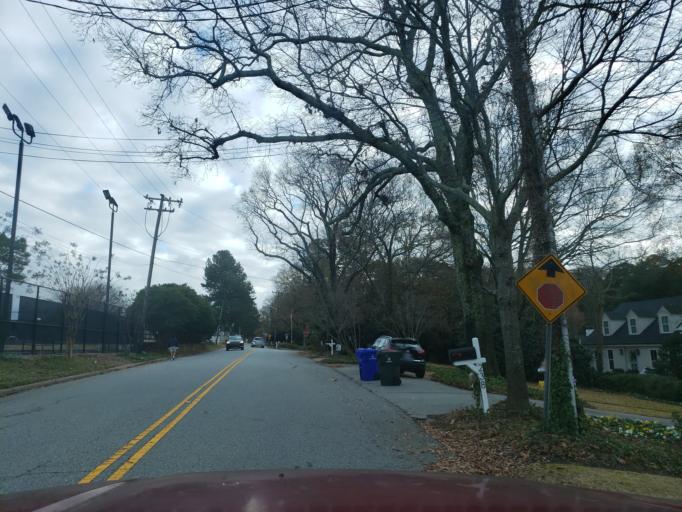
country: US
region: South Carolina
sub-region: Greenville County
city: Greenville
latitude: 34.8169
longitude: -82.3805
